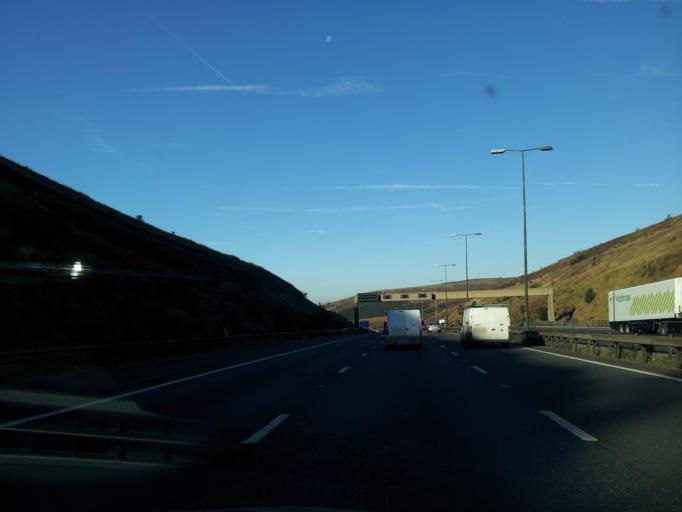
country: GB
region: England
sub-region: Borough of Oldham
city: Delph
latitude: 53.6292
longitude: -2.0309
